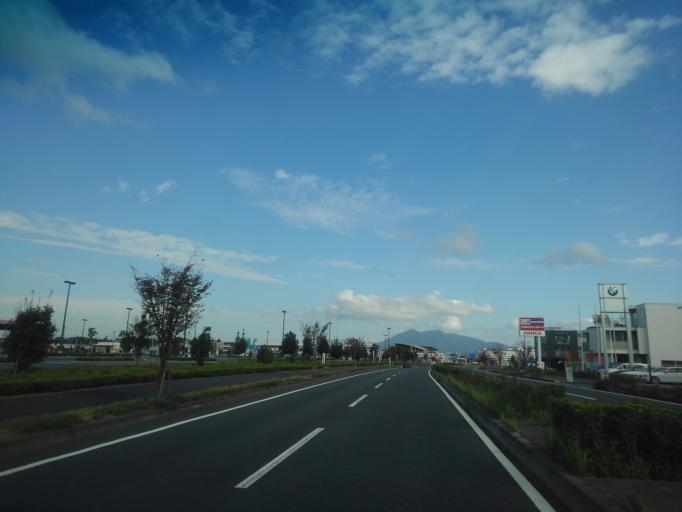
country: JP
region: Ibaraki
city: Naka
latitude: 36.0956
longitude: 140.0812
